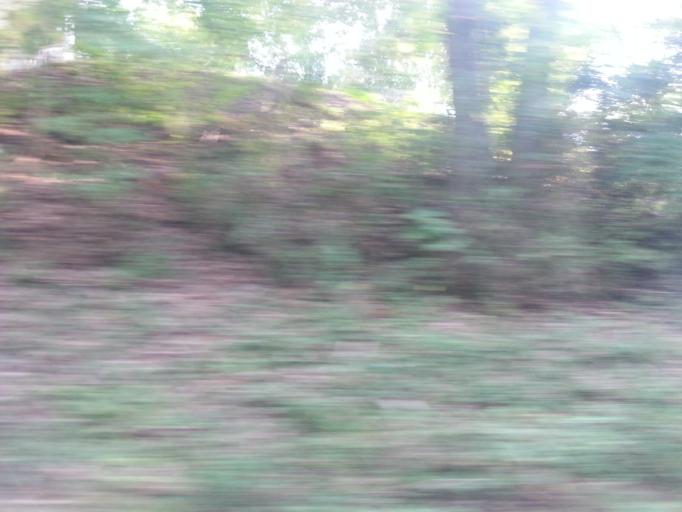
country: US
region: Tennessee
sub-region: Blount County
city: Alcoa
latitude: 35.7989
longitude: -83.9636
